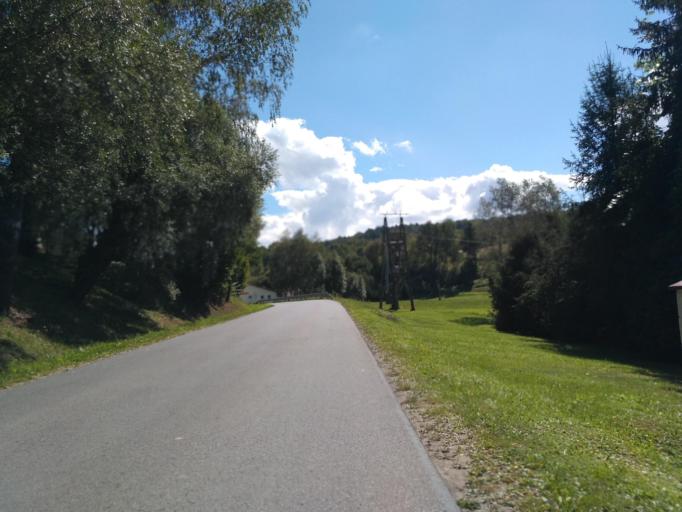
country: PL
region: Subcarpathian Voivodeship
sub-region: Powiat jasielski
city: Skolyszyn
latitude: 49.7926
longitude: 21.3277
